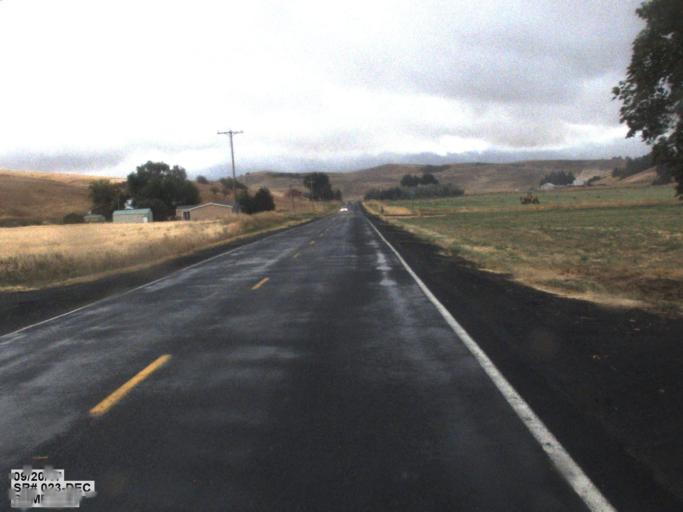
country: US
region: Washington
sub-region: Whitman County
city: Colfax
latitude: 47.0499
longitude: -117.5173
